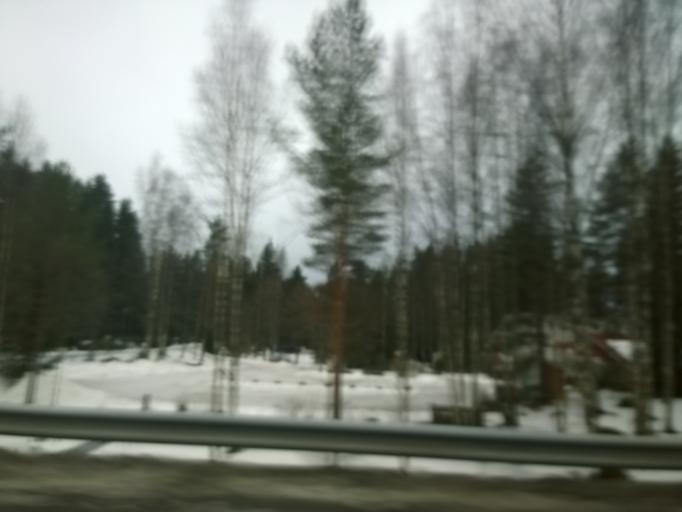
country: FI
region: Pirkanmaa
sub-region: Tampere
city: Lempaeaelae
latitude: 61.3641
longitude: 23.7837
